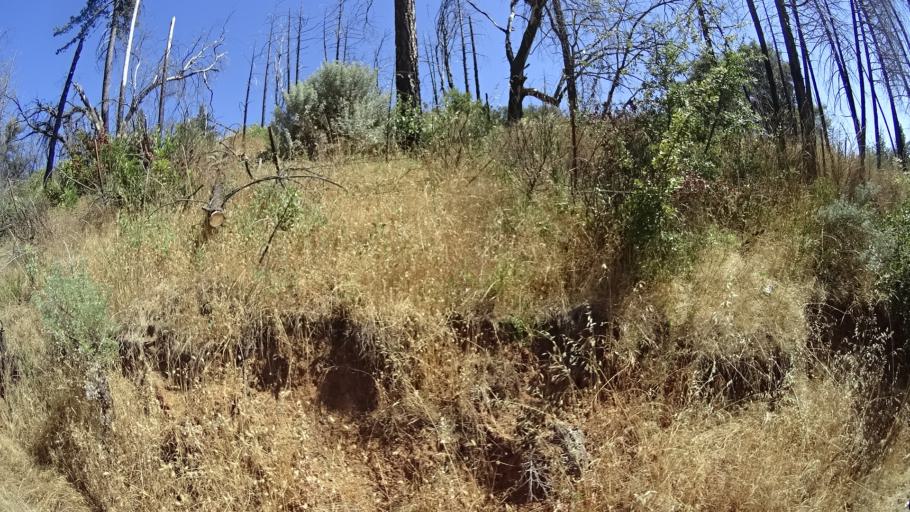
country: US
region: California
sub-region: Calaveras County
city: Mountain Ranch
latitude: 38.2746
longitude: -120.5892
